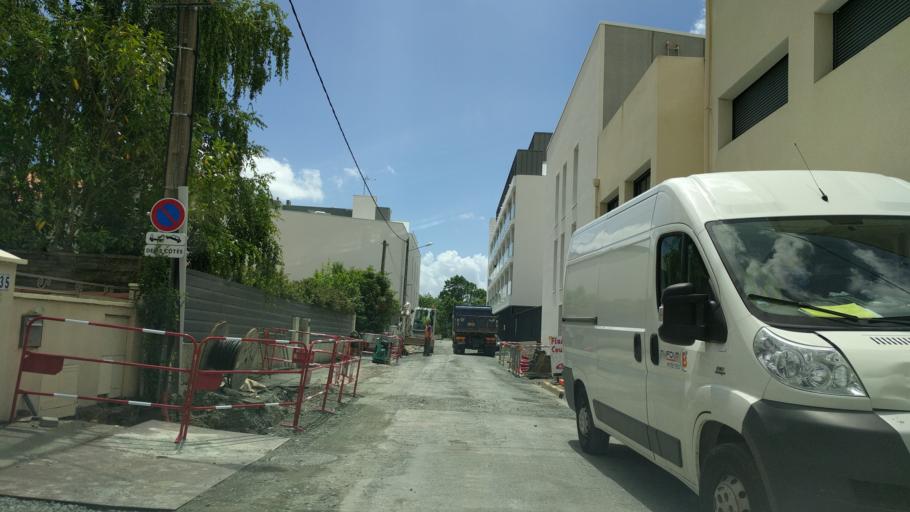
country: FR
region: Poitou-Charentes
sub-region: Departement de la Charente-Maritime
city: La Rochelle
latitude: 46.1594
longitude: -1.1355
